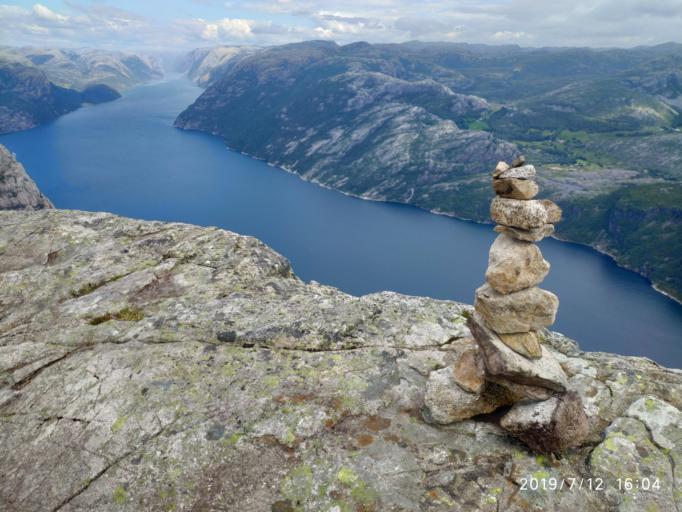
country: NO
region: Rogaland
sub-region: Forsand
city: Forsand
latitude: 58.9851
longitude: 6.1869
